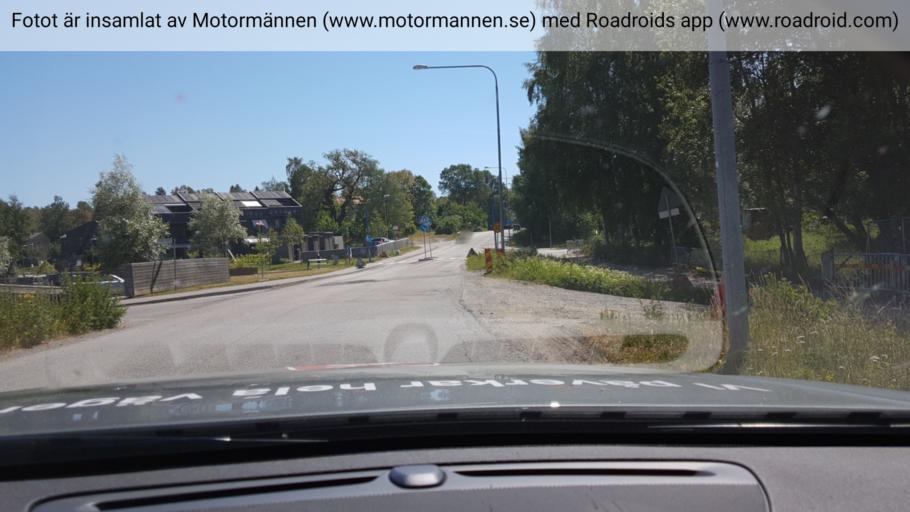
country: SE
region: Stockholm
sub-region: Huddinge Kommun
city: Huddinge
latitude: 59.2340
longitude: 17.9970
